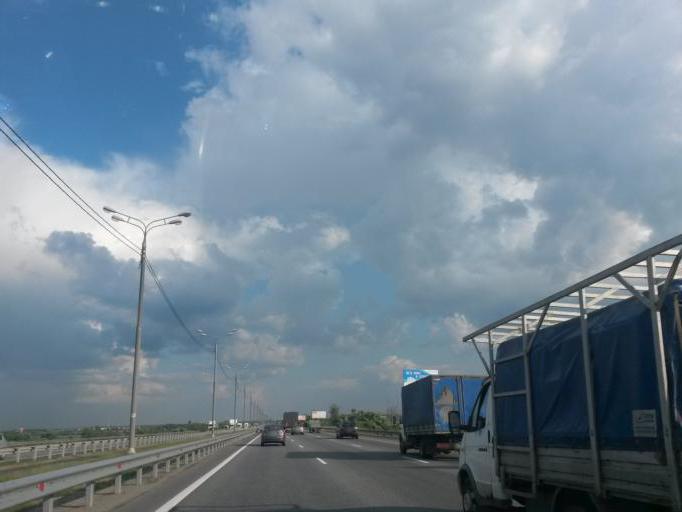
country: RU
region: Moskovskaya
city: Yam
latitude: 55.5029
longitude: 37.7246
